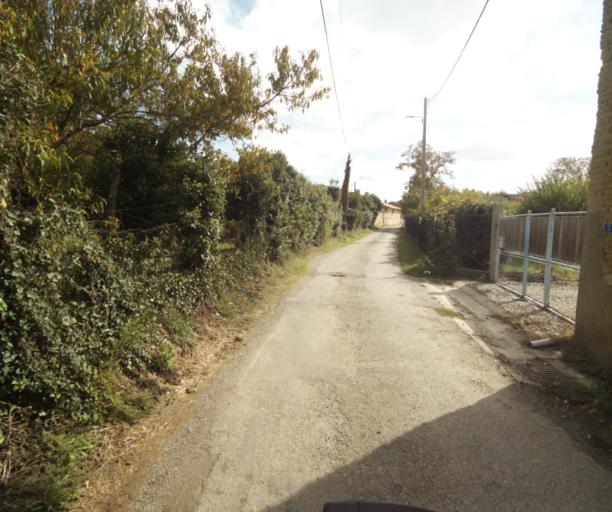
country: FR
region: Midi-Pyrenees
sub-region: Departement du Tarn-et-Garonne
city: Finhan
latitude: 43.9160
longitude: 1.2176
